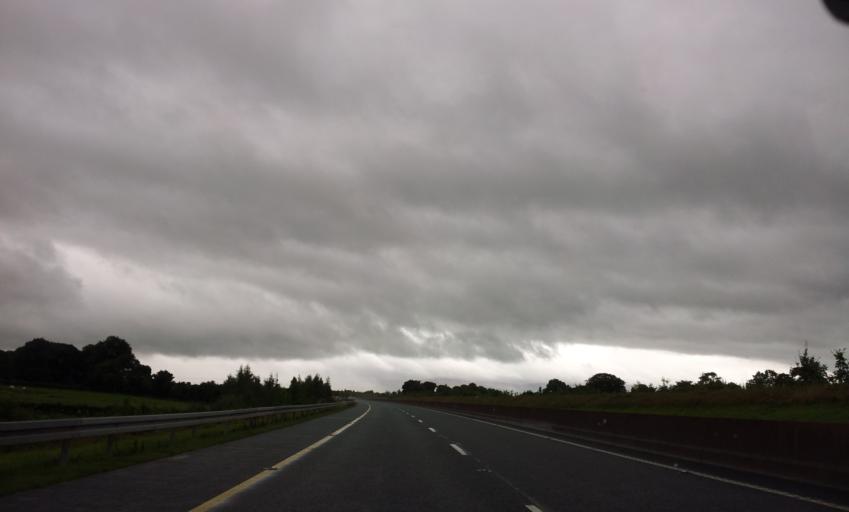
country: IE
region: Munster
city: Cashel
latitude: 52.4876
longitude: -7.9018
